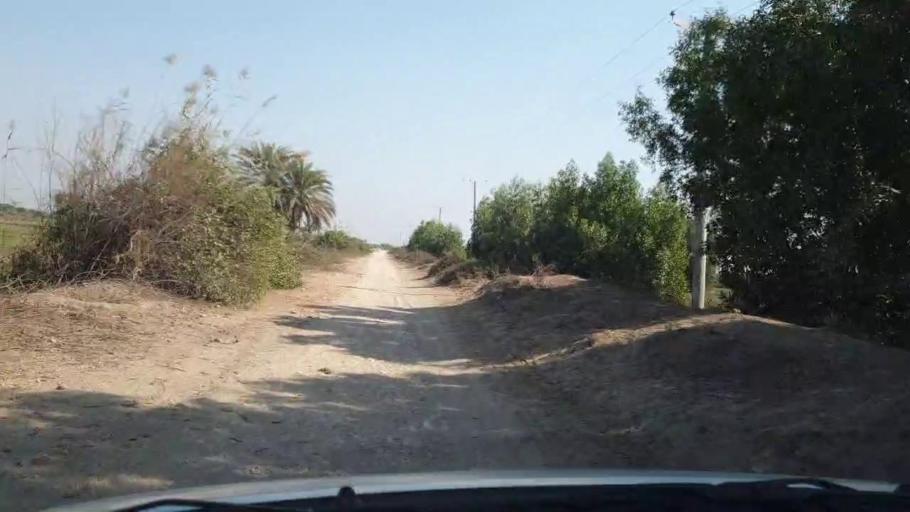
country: PK
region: Sindh
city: Gharo
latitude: 24.6500
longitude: 67.6240
